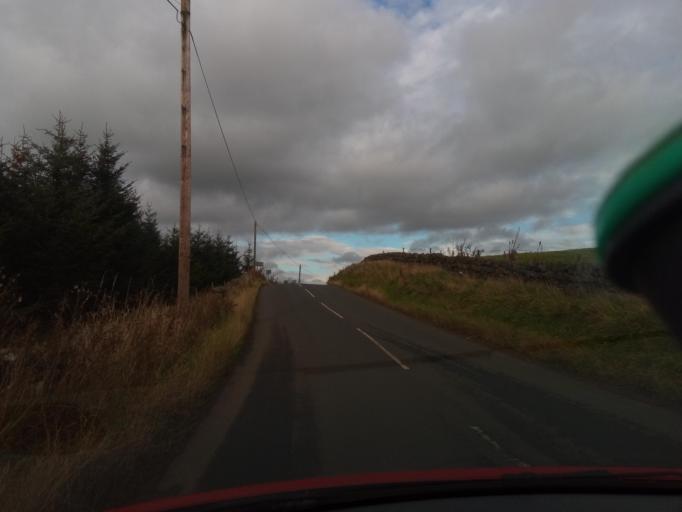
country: GB
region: Scotland
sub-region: South Lanarkshire
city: Carnwath
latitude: 55.7511
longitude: -3.6051
